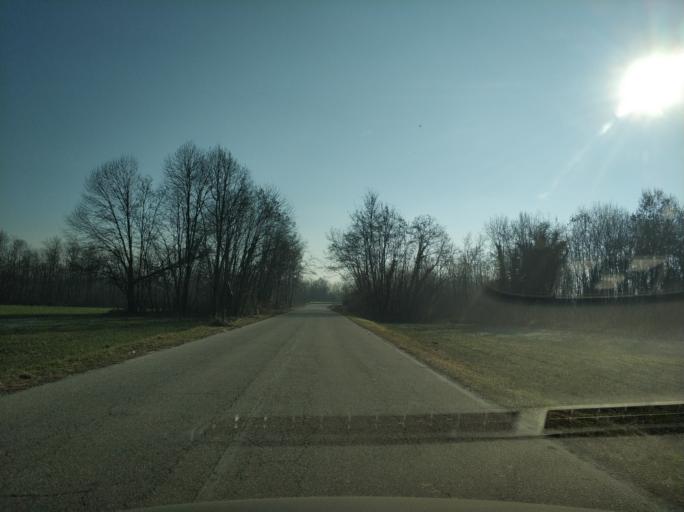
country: IT
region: Piedmont
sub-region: Provincia di Torino
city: Levone
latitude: 45.3088
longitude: 7.6136
